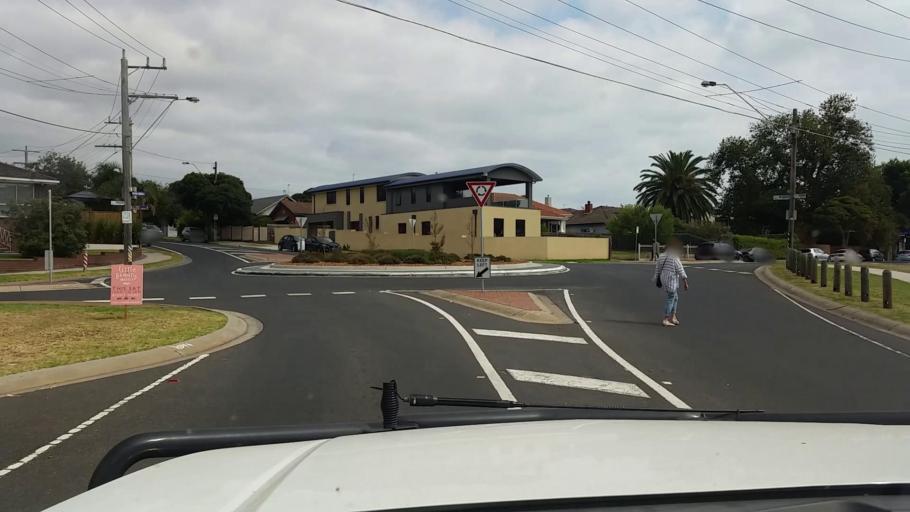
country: AU
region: Victoria
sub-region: Frankston
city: Frankston
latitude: -38.1484
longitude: 145.1210
